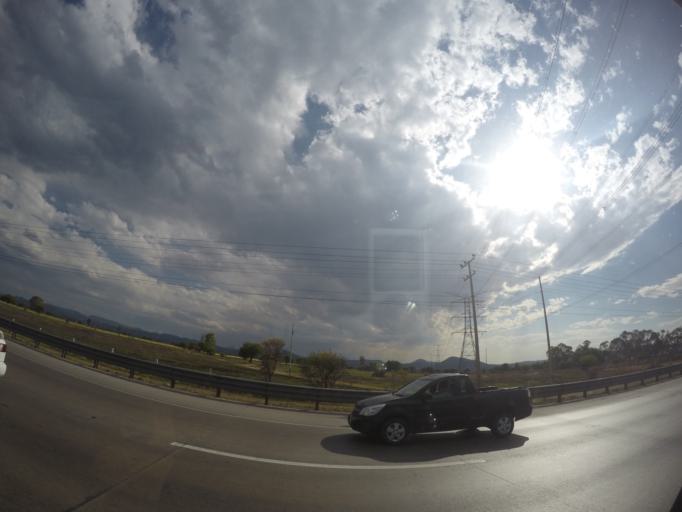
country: MX
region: Queretaro
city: El Sauz
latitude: 20.4789
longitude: -100.1120
